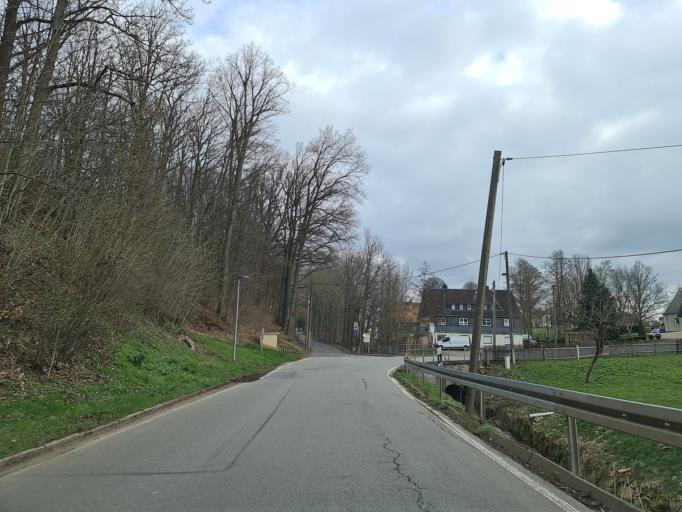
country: DE
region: Saxony
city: Wildenfels
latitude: 50.6995
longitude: 12.6176
